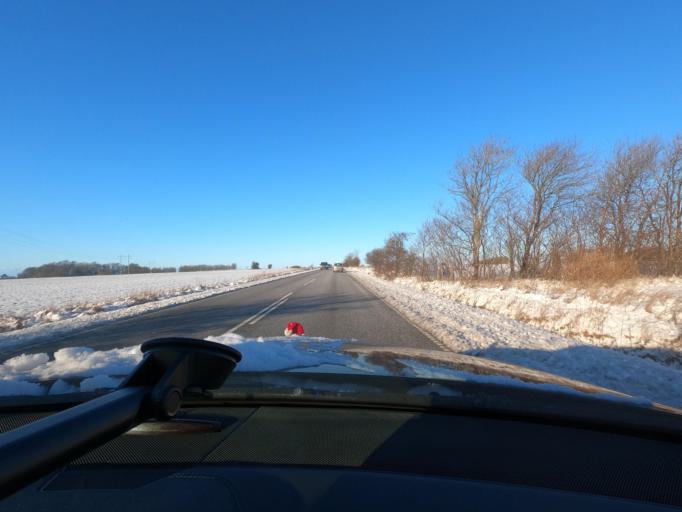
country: DK
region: South Denmark
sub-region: Aabenraa Kommune
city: Rodekro
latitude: 55.0997
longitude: 9.1896
